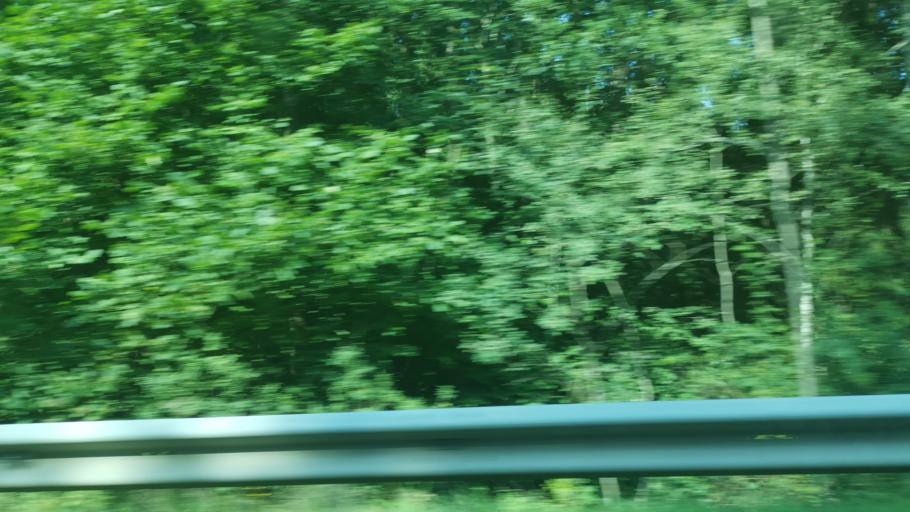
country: DE
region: Bavaria
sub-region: Upper Palatinate
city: Pemfling
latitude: 49.2878
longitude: 12.6263
